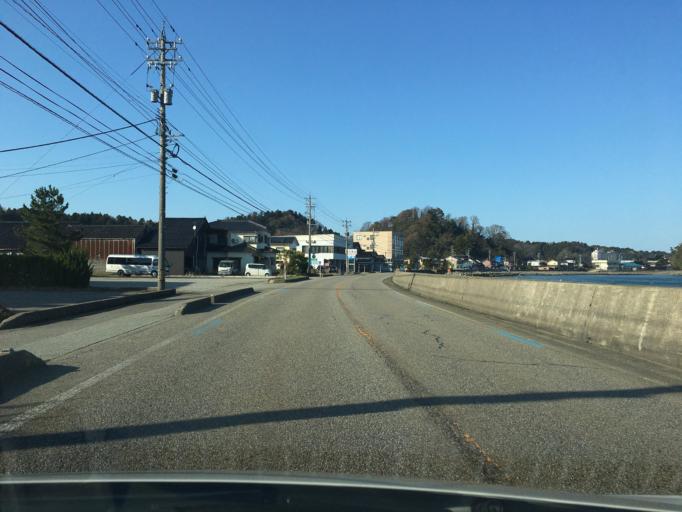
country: JP
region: Toyama
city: Himi
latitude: 36.8766
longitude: 136.9846
